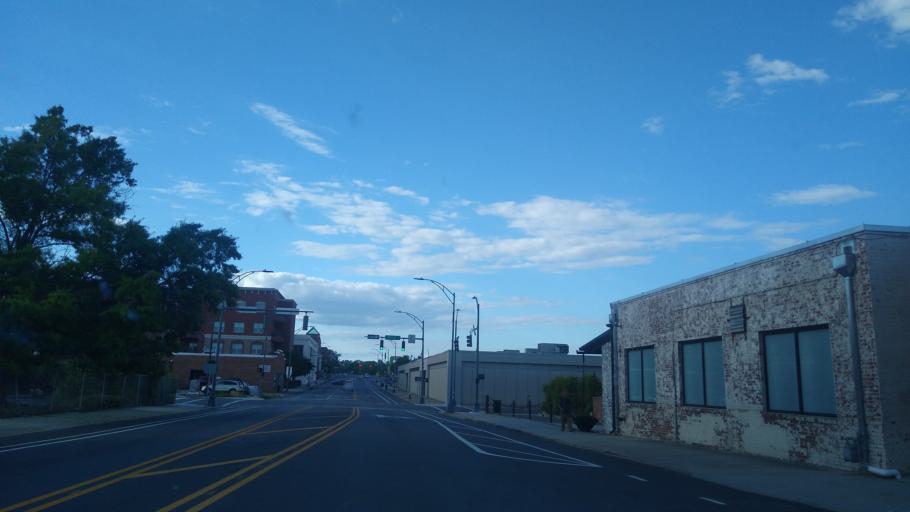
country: US
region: North Carolina
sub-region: Guilford County
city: Greensboro
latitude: 36.0717
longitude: -79.7869
